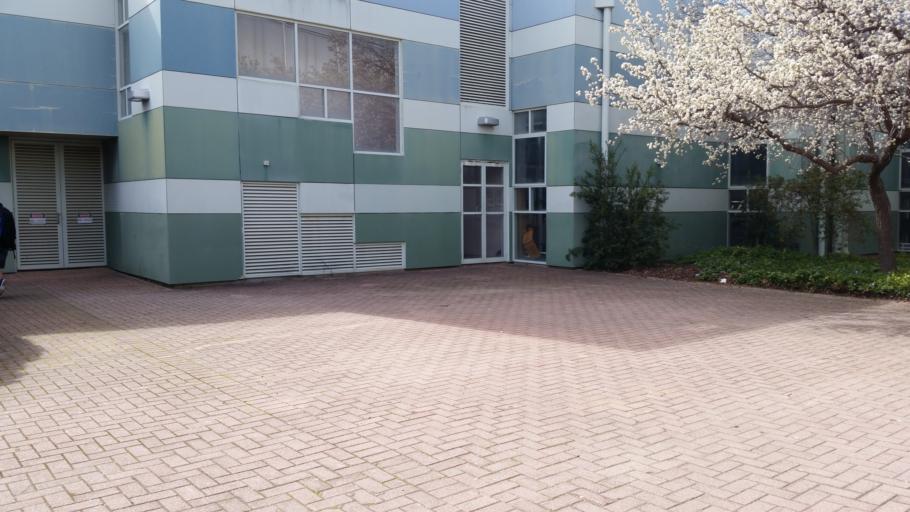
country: AU
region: Australian Capital Territory
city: Kaleen
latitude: -35.2463
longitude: 149.1033
